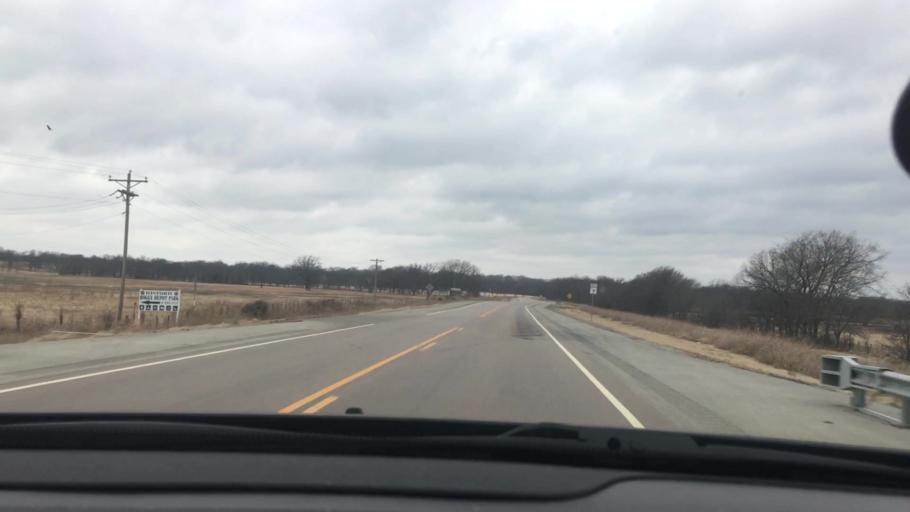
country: US
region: Oklahoma
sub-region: Atoka County
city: Atoka
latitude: 34.3688
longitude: -96.3233
